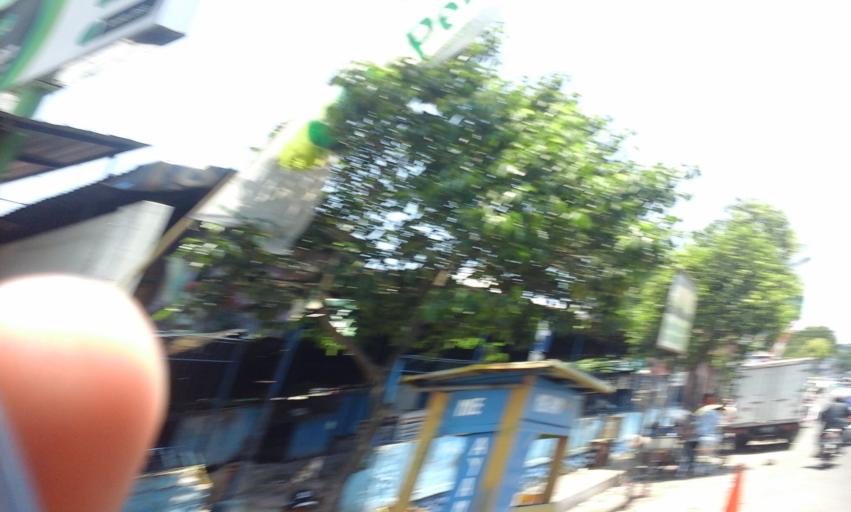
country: ID
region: East Java
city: Kepatihan
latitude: -8.1766
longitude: 113.7045
